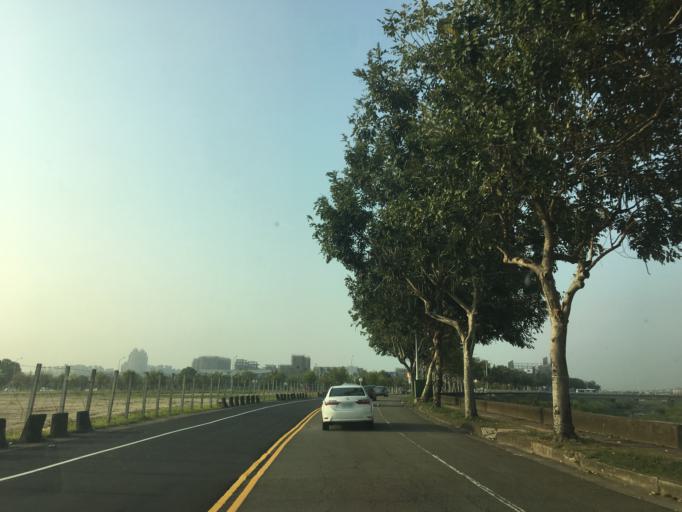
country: TW
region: Taiwan
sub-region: Taichung City
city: Taichung
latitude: 24.1766
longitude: 120.7095
